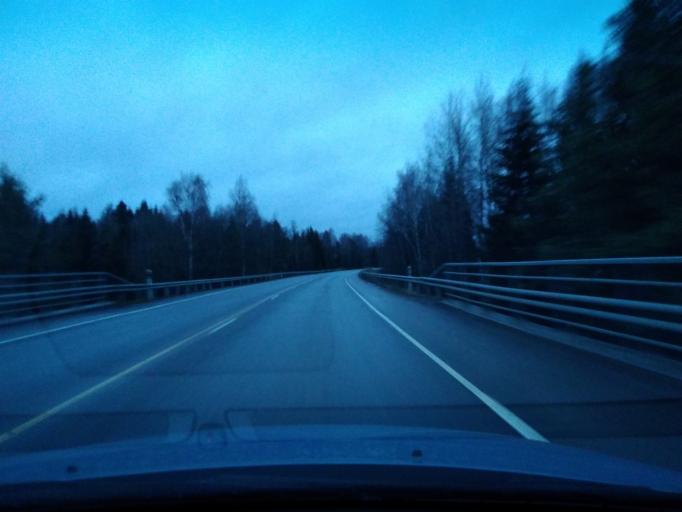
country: FI
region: Uusimaa
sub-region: Porvoo
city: Porvoo
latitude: 60.4081
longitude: 25.5850
